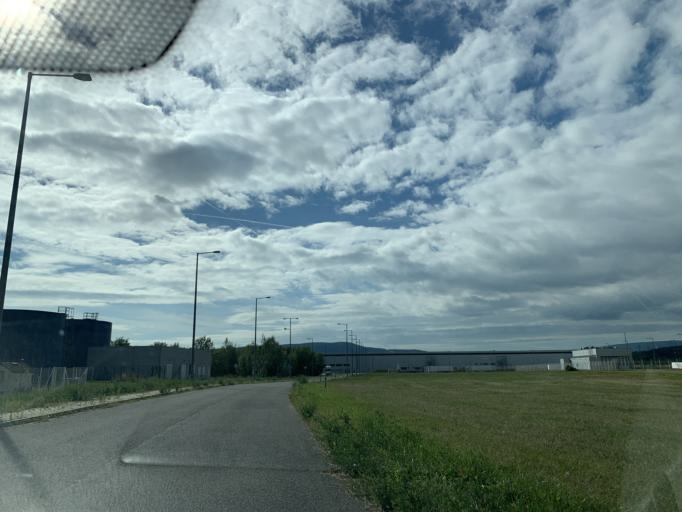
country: SK
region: Trenciansky
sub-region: Okres Nove Mesto nad Vahom
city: Nove Mesto nad Vahom
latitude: 48.7654
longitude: 17.8824
